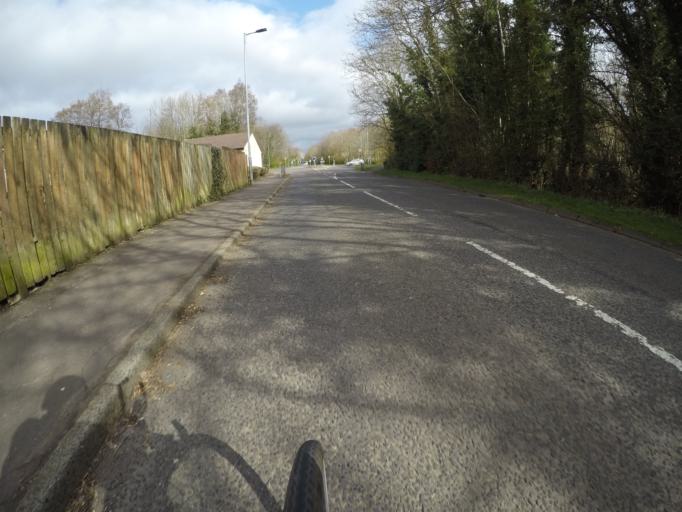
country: GB
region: Scotland
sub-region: North Ayrshire
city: Irvine
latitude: 55.6308
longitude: -4.6362
